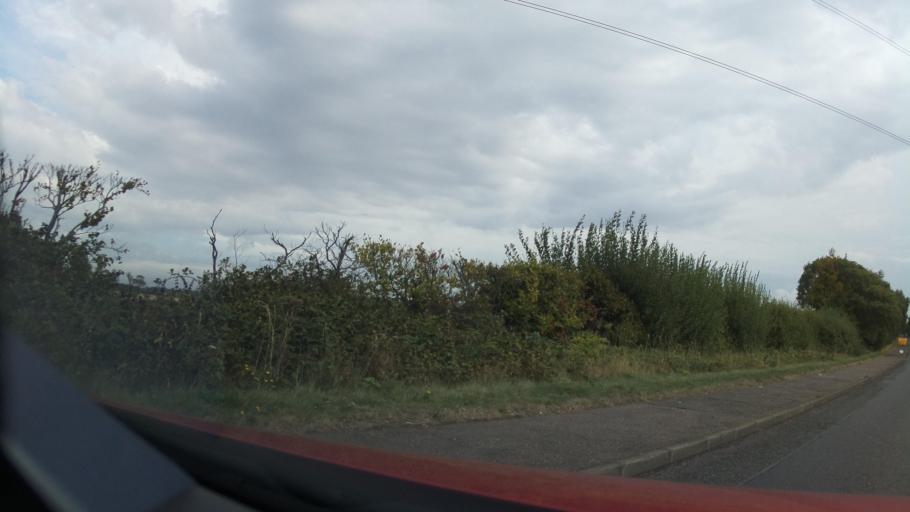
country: GB
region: Scotland
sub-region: East Lothian
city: Cockenzie
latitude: 55.9605
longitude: -2.9561
